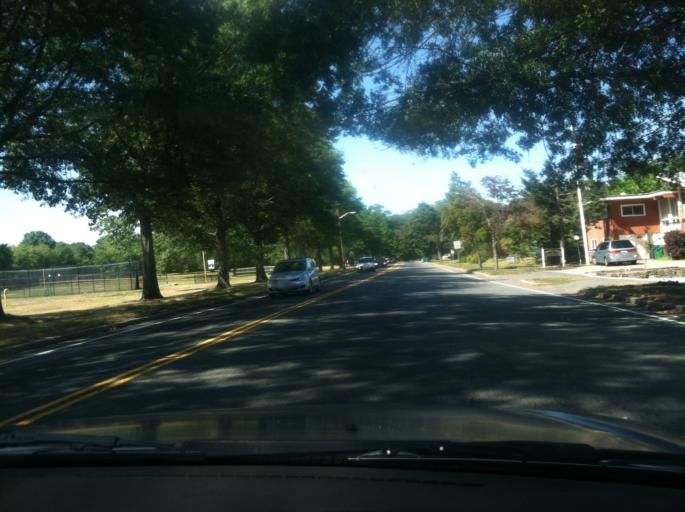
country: US
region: Massachusetts
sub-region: Suffolk County
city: Chelsea
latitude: 42.3904
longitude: -71.0423
